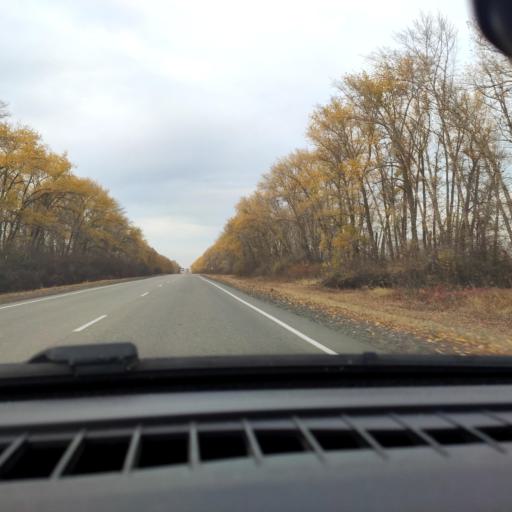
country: RU
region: Voronezj
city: Ostrogozhsk
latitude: 50.9902
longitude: 38.9977
